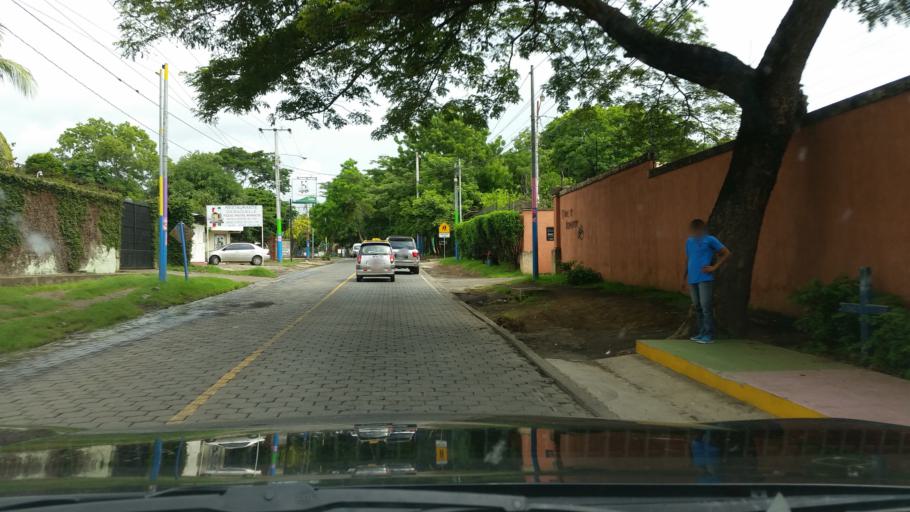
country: NI
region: Masaya
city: Ticuantepe
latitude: 12.0535
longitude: -86.2031
